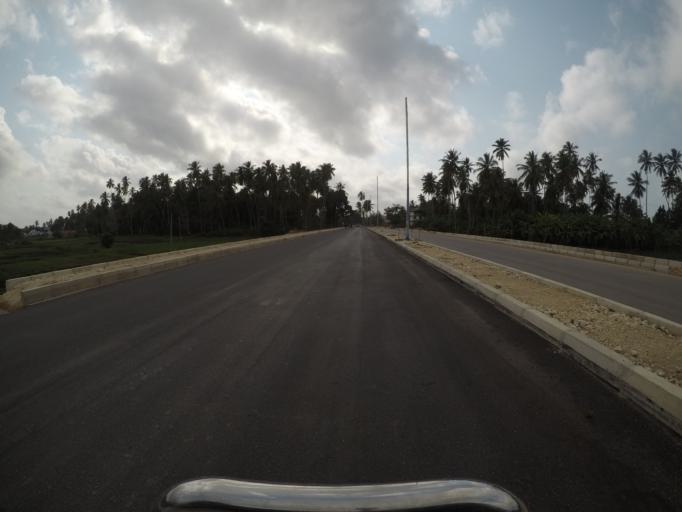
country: TZ
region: Zanzibar Central/South
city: Koani
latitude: -6.1959
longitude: 39.2755
